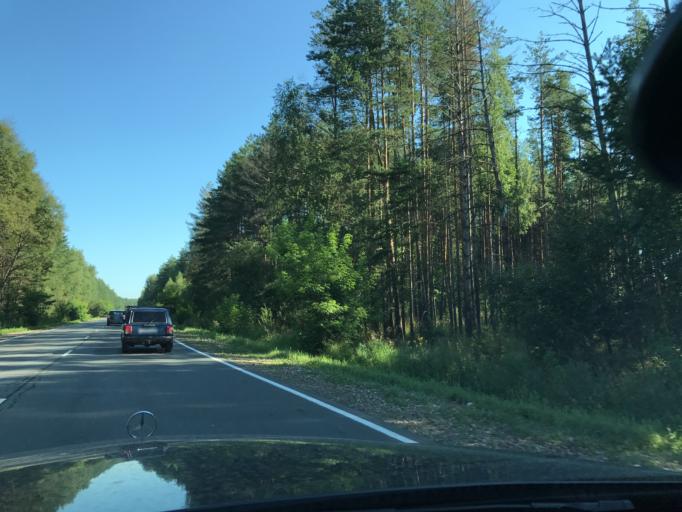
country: RU
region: Moskovskaya
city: Noginsk-9
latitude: 56.0932
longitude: 38.5808
